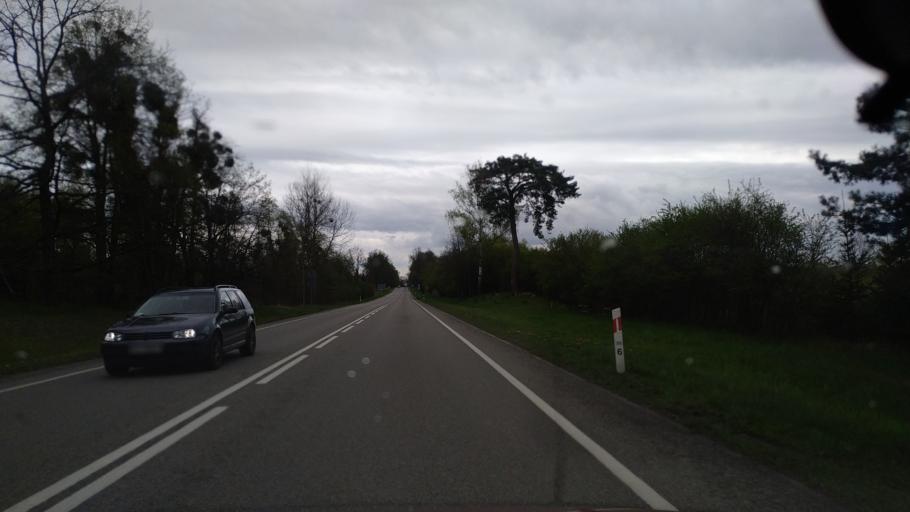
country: PL
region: Pomeranian Voivodeship
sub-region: Powiat starogardzki
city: Starogard Gdanski
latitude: 53.9980
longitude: 18.5901
